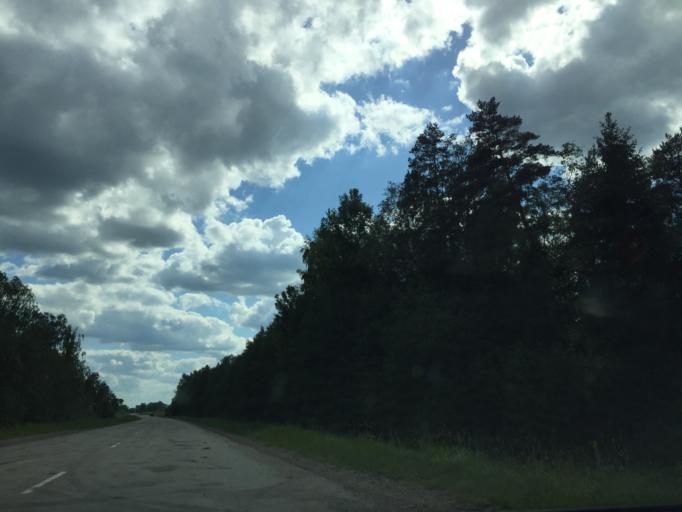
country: LV
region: Jaunpils
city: Jaunpils
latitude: 56.8646
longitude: 23.0584
